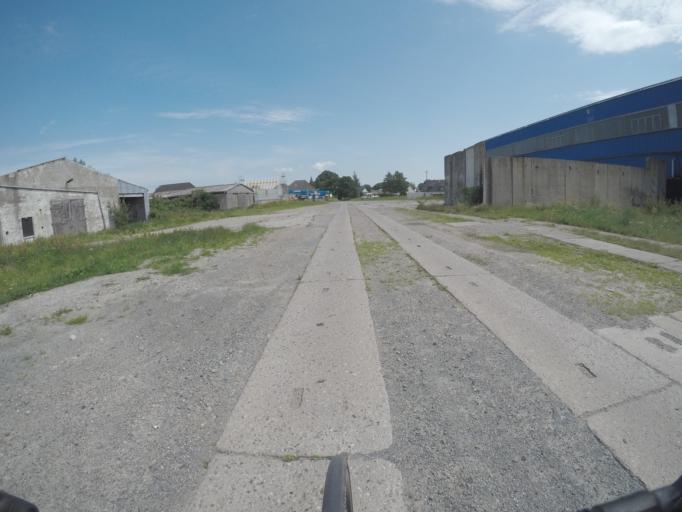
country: DE
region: Mecklenburg-Vorpommern
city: Rambin
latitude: 54.3563
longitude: 13.1990
